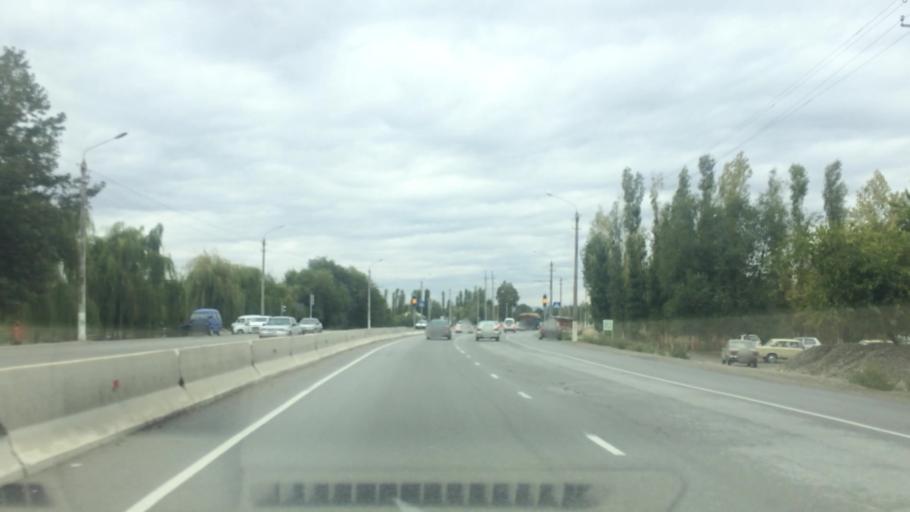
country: UZ
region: Jizzax
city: Jizzax
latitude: 39.9897
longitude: 67.5820
